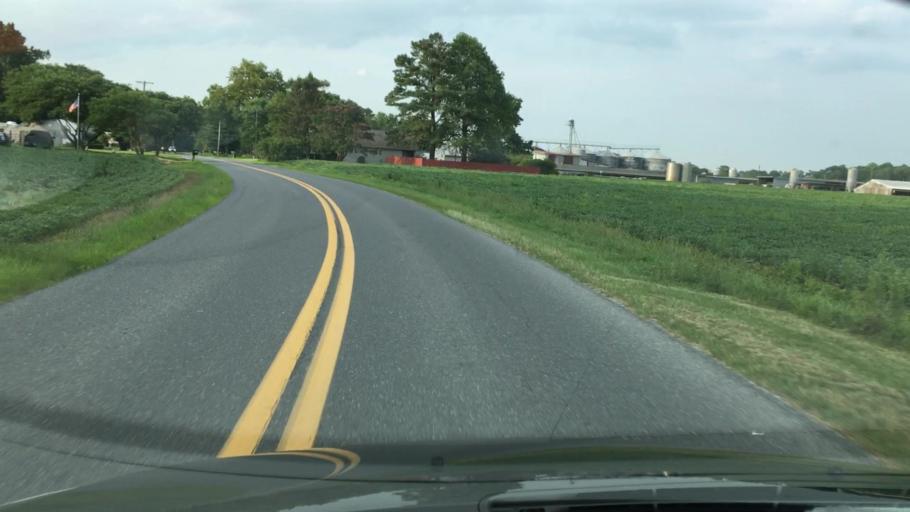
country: US
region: Maryland
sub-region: Worcester County
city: Ocean Pines
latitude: 38.4717
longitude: -75.1399
